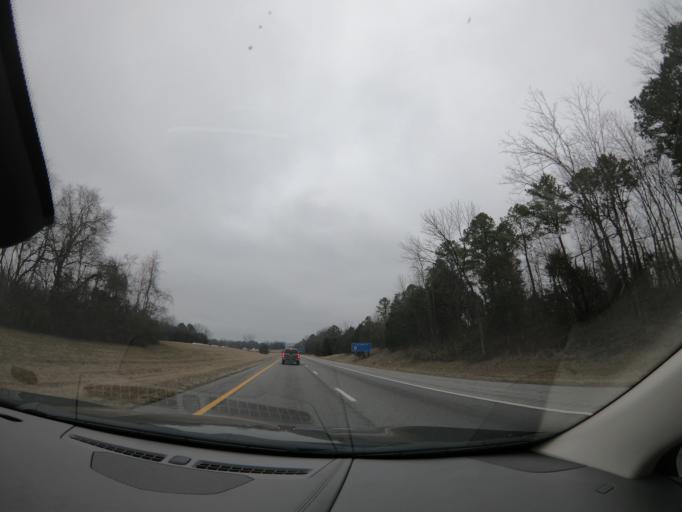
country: US
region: Tennessee
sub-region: Rutherford County
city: Plainview
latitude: 35.6040
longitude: -86.2395
